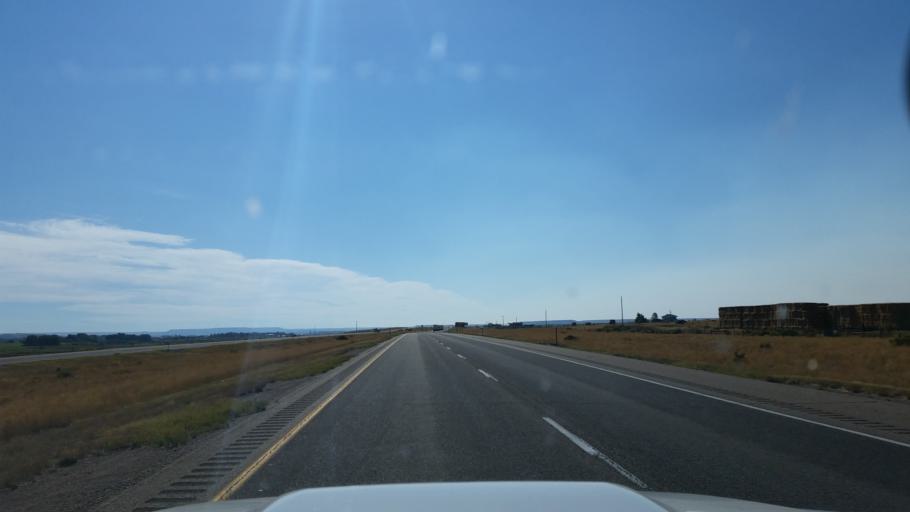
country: US
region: Wyoming
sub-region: Uinta County
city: Lyman
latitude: 41.3726
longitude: -110.2574
